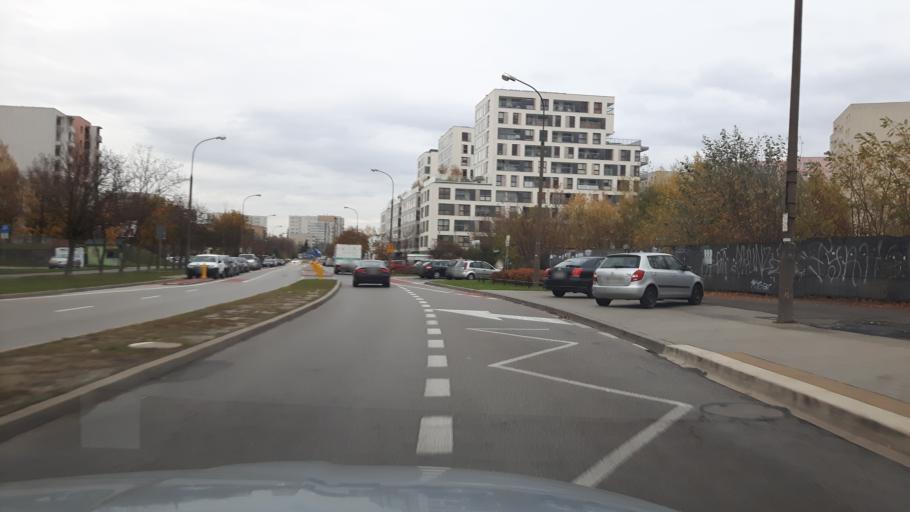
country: PL
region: Masovian Voivodeship
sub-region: Warszawa
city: Ursynow
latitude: 52.1508
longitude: 21.0484
